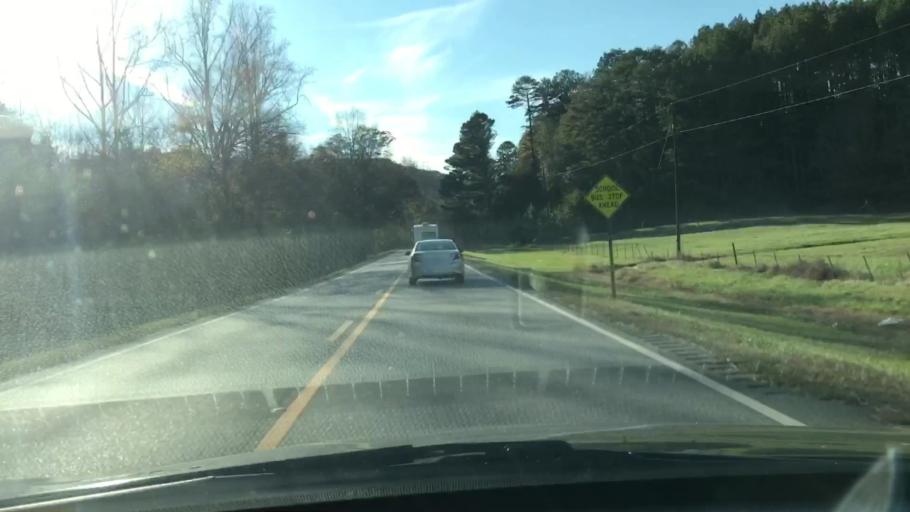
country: US
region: Alabama
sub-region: Cleburne County
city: Heflin
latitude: 33.6506
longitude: -85.5409
